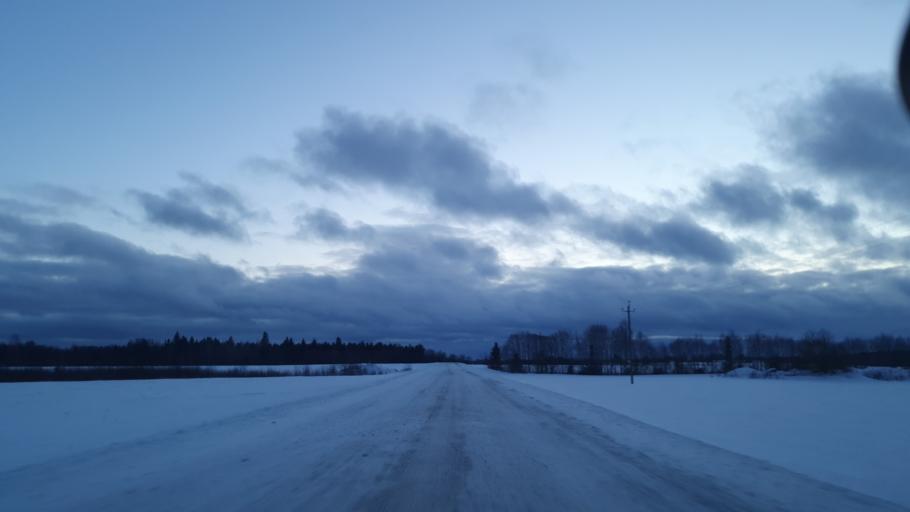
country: EE
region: Jogevamaa
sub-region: Jogeva linn
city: Jogeva
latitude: 58.6174
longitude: 26.4132
